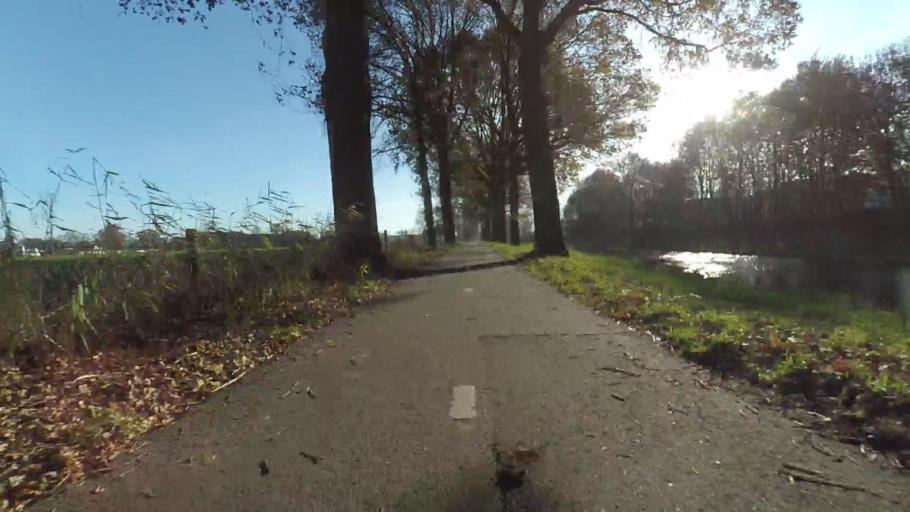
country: NL
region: Utrecht
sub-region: Gemeente Woudenberg
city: Woudenberg
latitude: 52.0829
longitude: 5.4551
